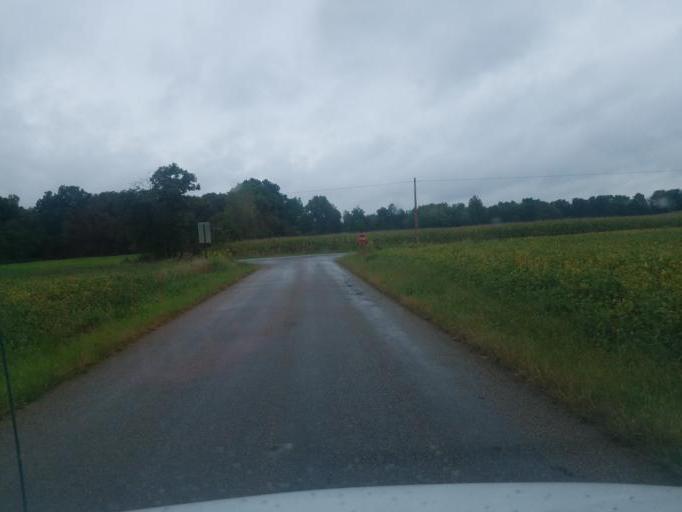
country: US
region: Ohio
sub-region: Wayne County
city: West Salem
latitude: 40.9415
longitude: -82.1167
